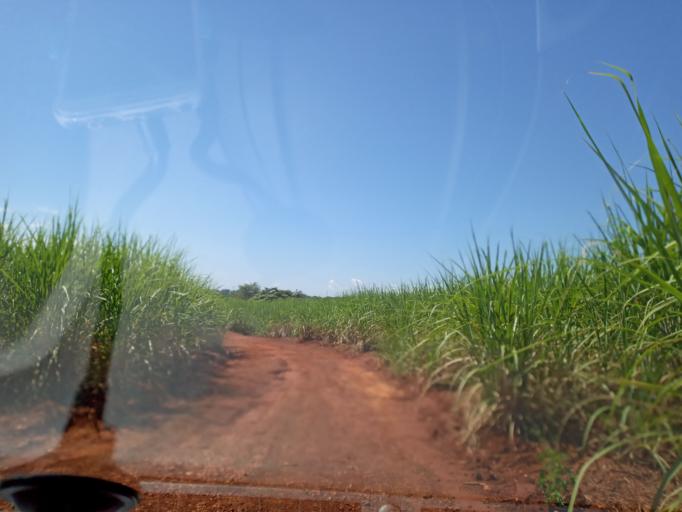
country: BR
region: Goias
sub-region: Itumbiara
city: Itumbiara
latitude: -18.4328
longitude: -49.1506
